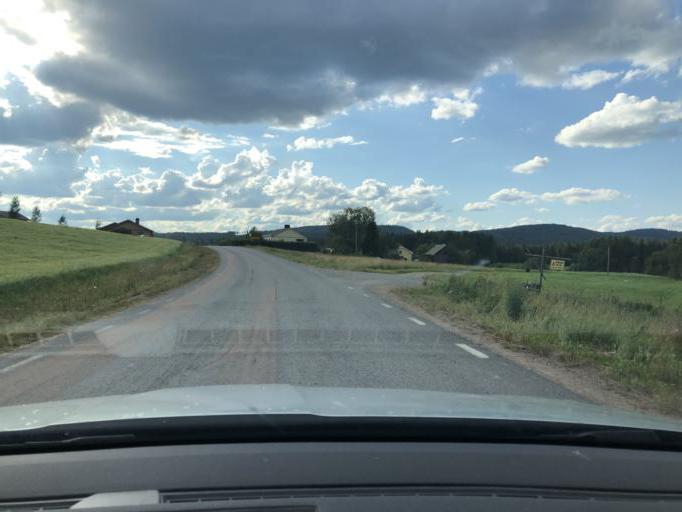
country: SE
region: Vaesternorrland
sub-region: Solleftea Kommun
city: Solleftea
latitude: 63.2055
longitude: 17.1336
